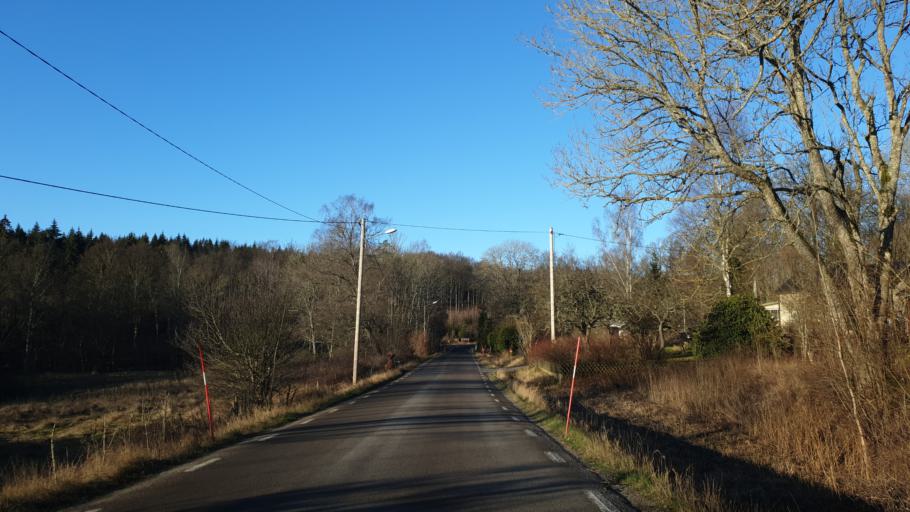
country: SE
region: Blekinge
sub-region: Karlskrona Kommun
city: Nattraby
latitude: 56.2312
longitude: 15.5192
